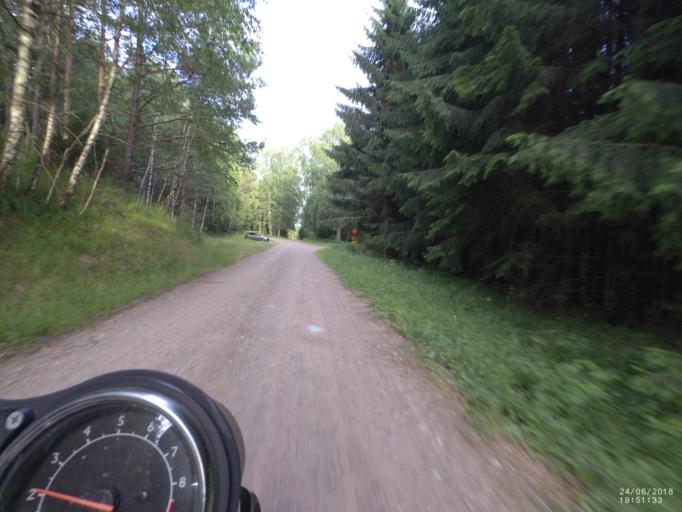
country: SE
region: Soedermanland
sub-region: Oxelosunds Kommun
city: Oxelosund
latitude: 58.7720
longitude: 17.1532
